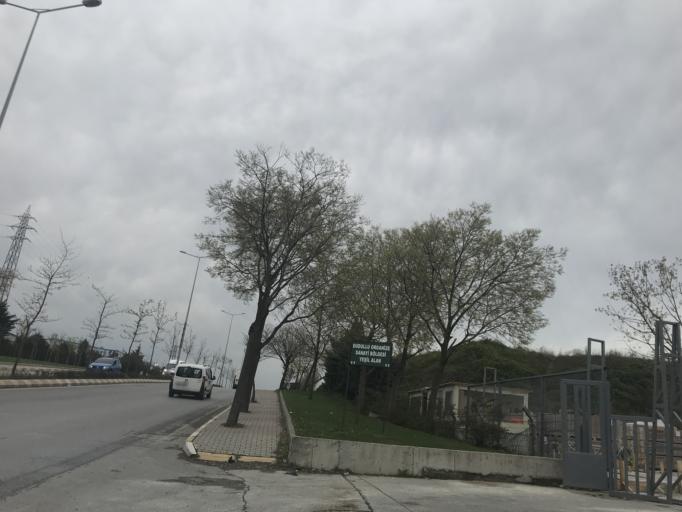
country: TR
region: Istanbul
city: Umraniye
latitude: 41.0027
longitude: 29.1721
